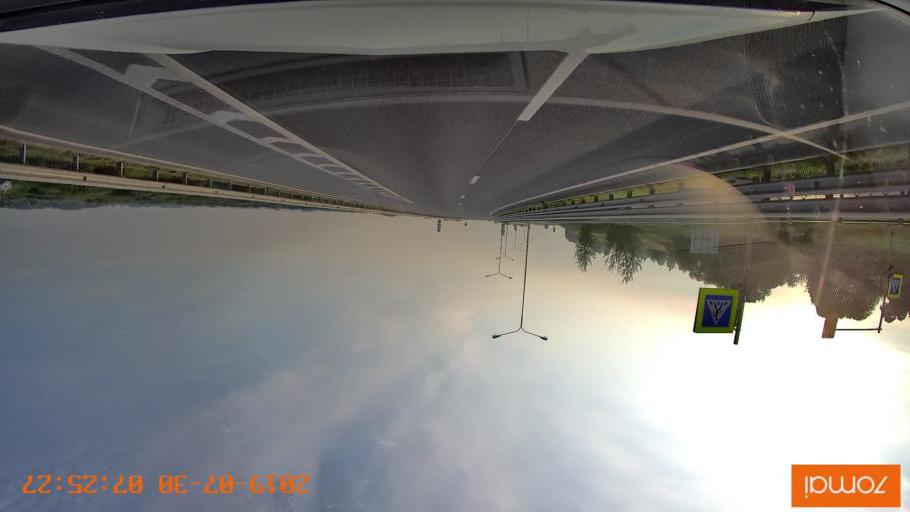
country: RU
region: Kaliningrad
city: Gvardeysk
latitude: 54.6866
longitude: 20.8355
